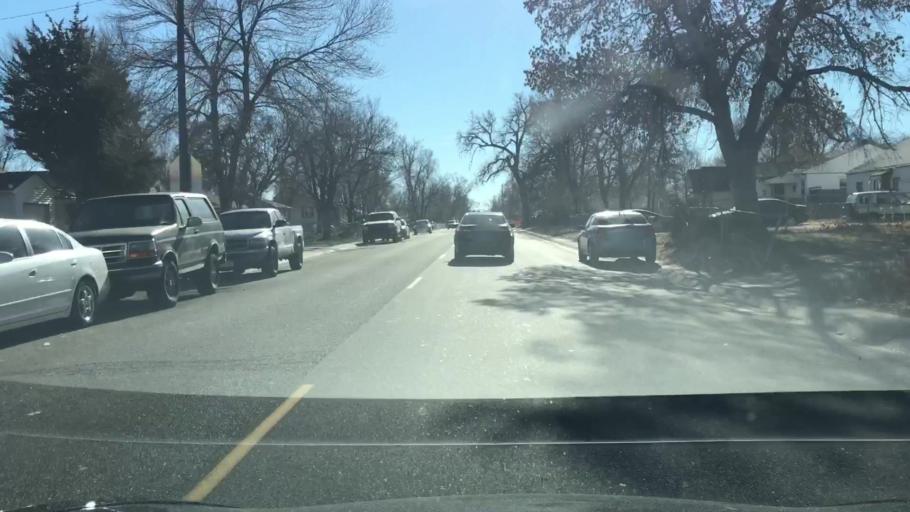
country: US
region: Colorado
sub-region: Adams County
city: Aurora
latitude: 39.7467
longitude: -104.8847
